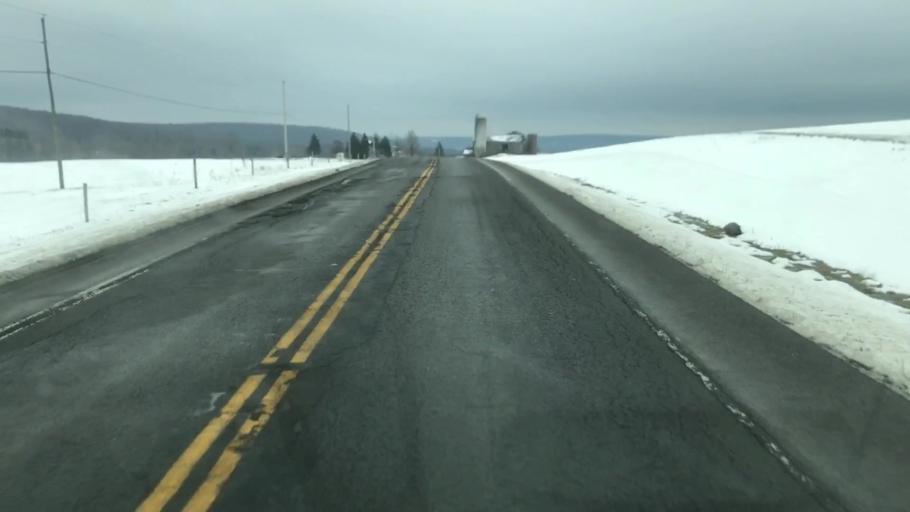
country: US
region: New York
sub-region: Cayuga County
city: Moravia
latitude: 42.7216
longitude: -76.3140
